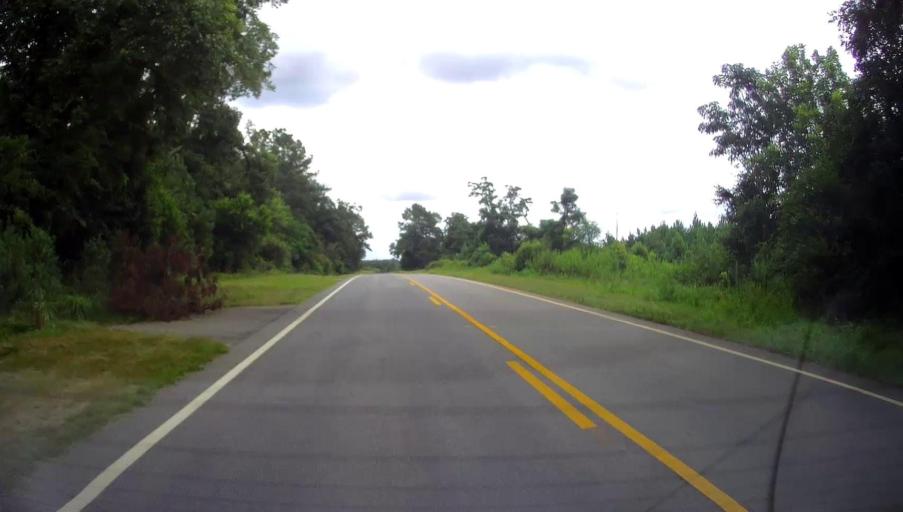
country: US
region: Georgia
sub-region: Macon County
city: Oglethorpe
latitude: 32.2739
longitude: -84.1249
